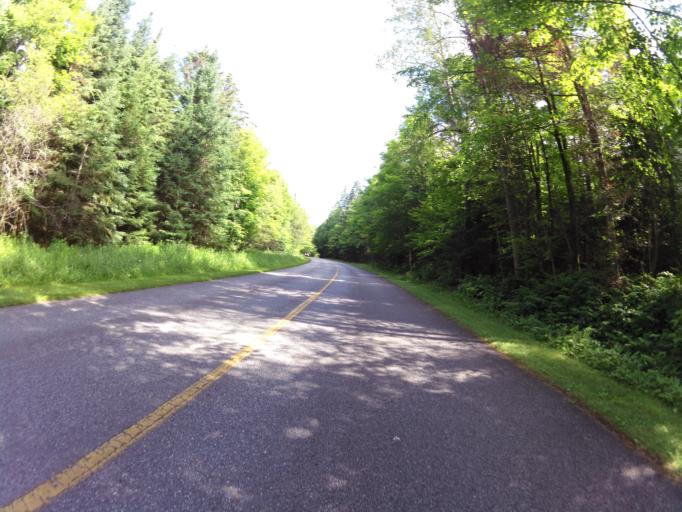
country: CA
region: Quebec
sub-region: Outaouais
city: Wakefield
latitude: 45.6222
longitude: -76.0088
